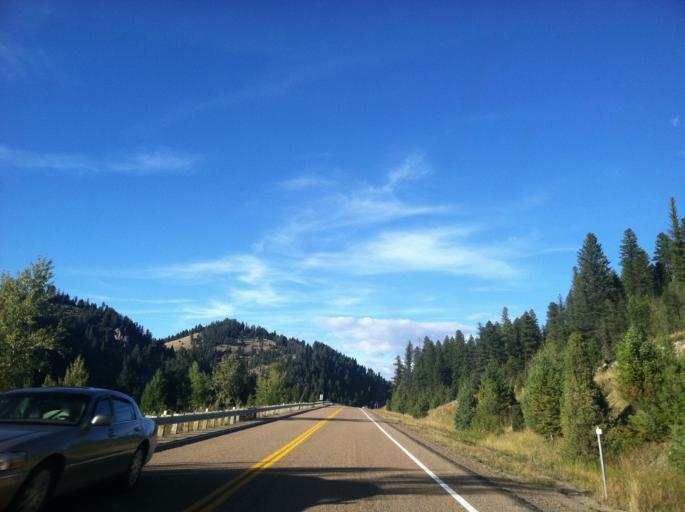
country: US
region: Montana
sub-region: Granite County
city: Philipsburg
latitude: 46.4448
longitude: -113.2528
